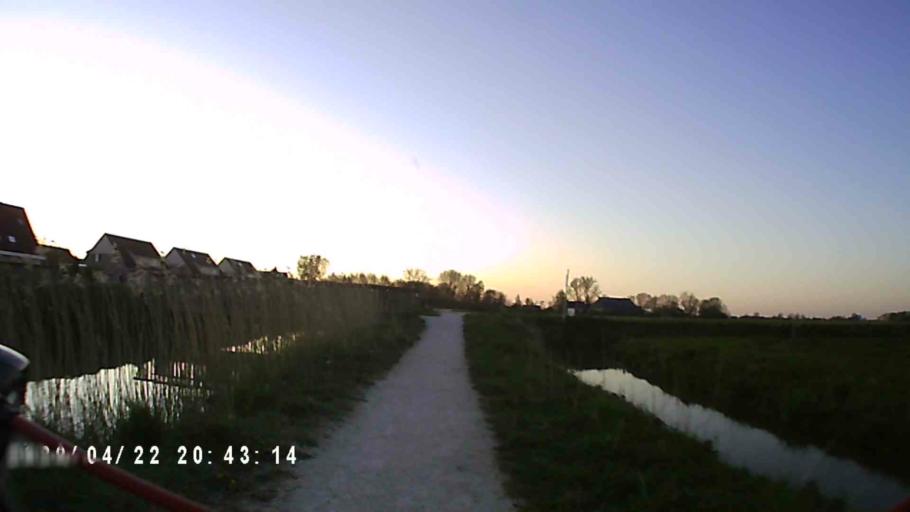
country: NL
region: Groningen
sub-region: Gemeente Winsum
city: Winsum
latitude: 53.3259
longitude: 6.5341
